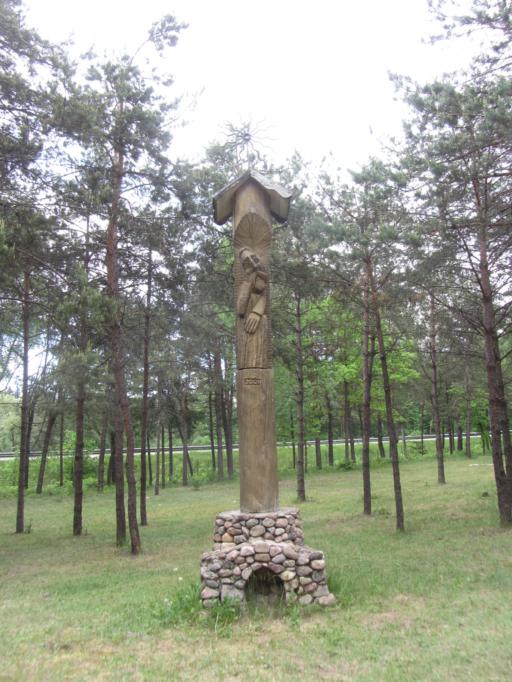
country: LT
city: Ziezmariai
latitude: 54.7990
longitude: 24.5318
